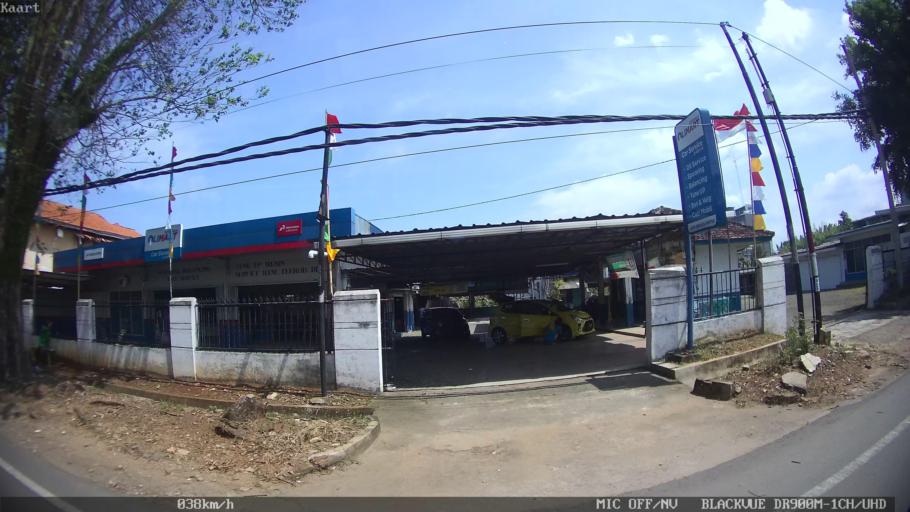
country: ID
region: Lampung
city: Kedaton
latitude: -5.3790
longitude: 105.2615
